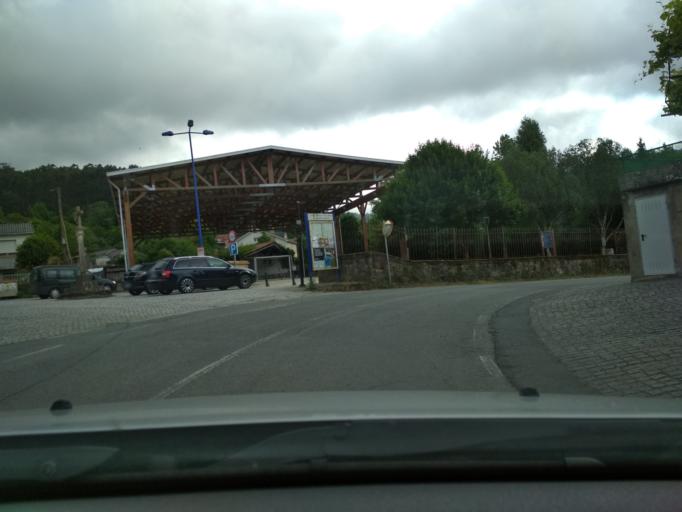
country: ES
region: Galicia
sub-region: Provincia da Coruna
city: Culleredo
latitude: 43.2498
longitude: -8.4073
